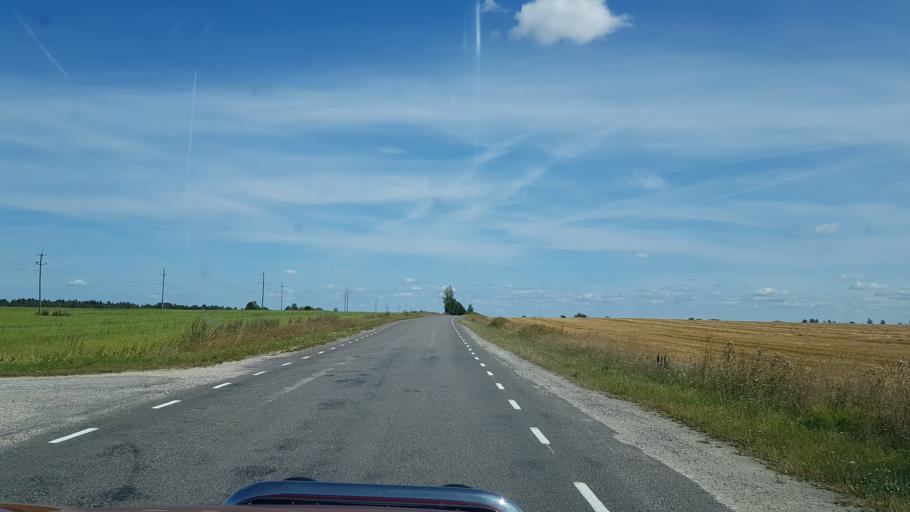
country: EE
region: Jaervamaa
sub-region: Jaerva-Jaani vald
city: Jarva-Jaani
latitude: 59.0427
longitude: 25.9769
